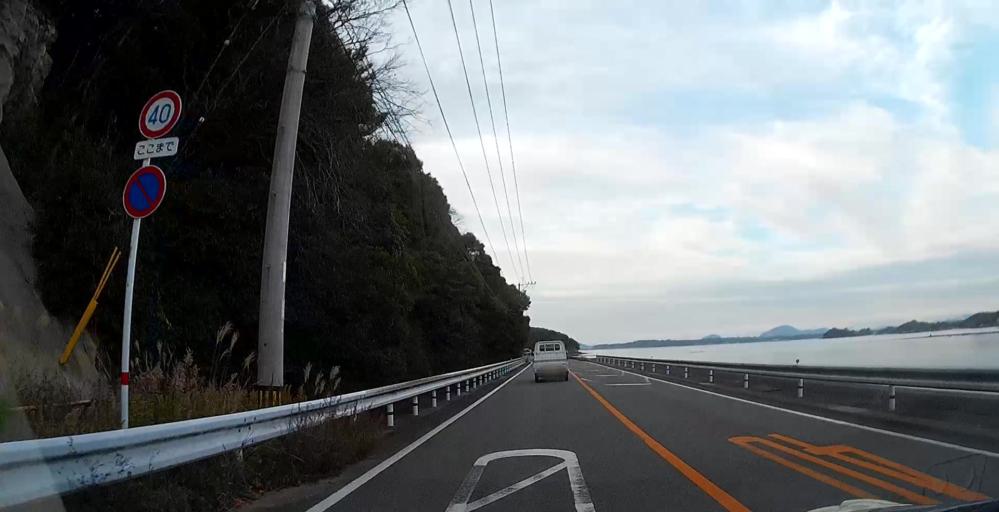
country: JP
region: Kumamoto
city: Hondo
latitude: 32.5014
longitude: 130.3906
